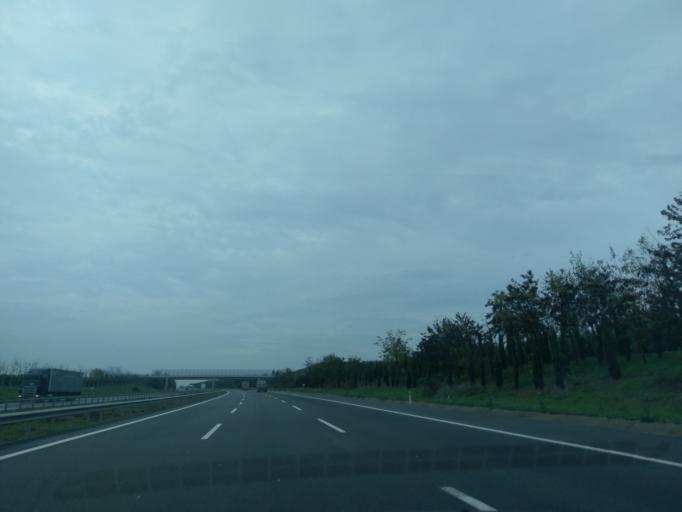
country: TR
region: Istanbul
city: Canta
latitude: 41.1589
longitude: 28.1385
